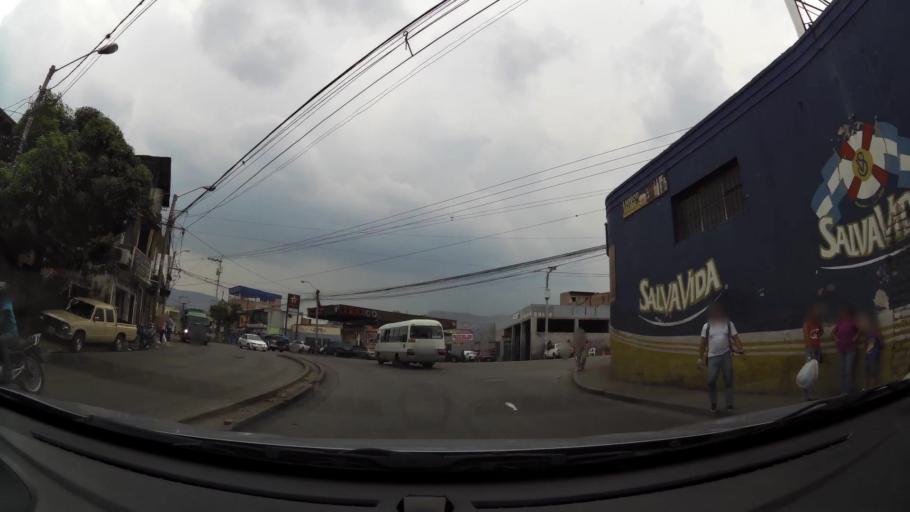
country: HN
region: Francisco Morazan
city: Tegucigalpa
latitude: 14.0958
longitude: -87.2170
